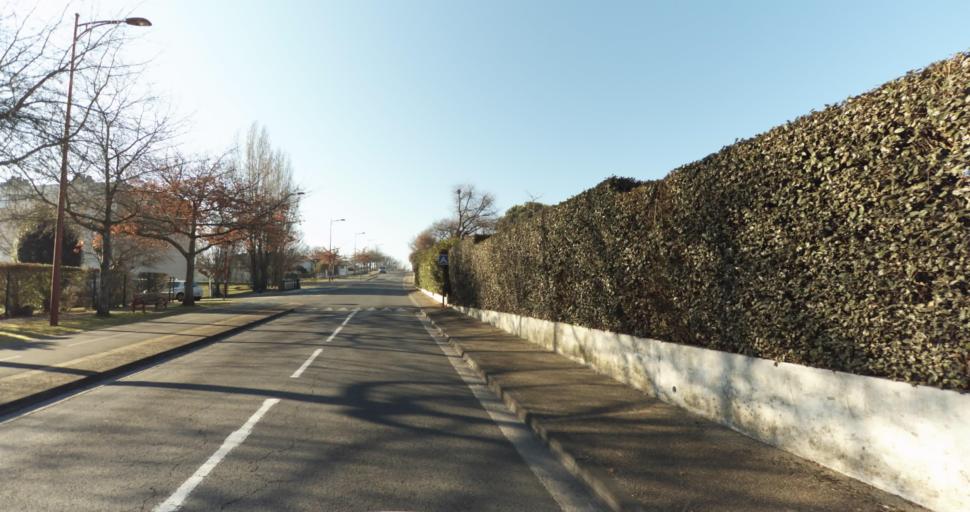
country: FR
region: Aquitaine
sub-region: Departement de la Gironde
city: Carbon-Blanc
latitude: 44.8927
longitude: -0.5071
